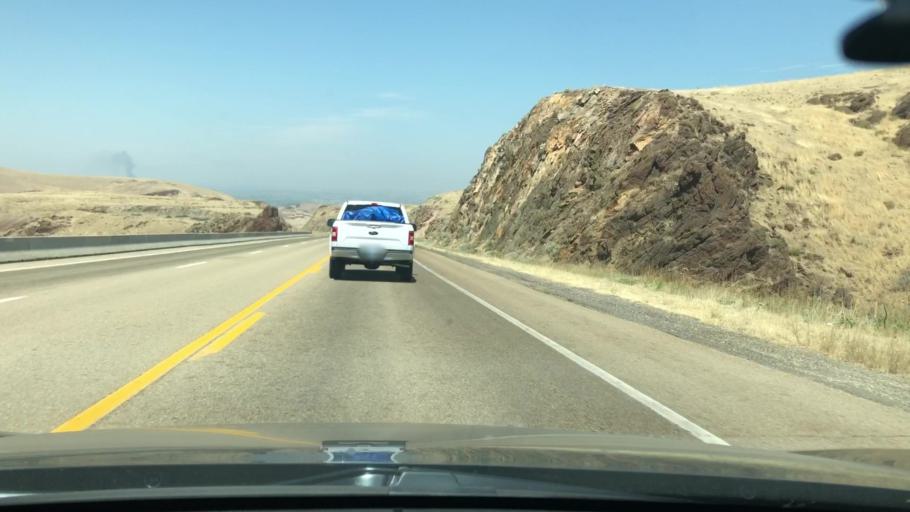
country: US
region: Idaho
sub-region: Owyhee County
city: Marsing
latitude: 43.4246
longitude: -116.8578
